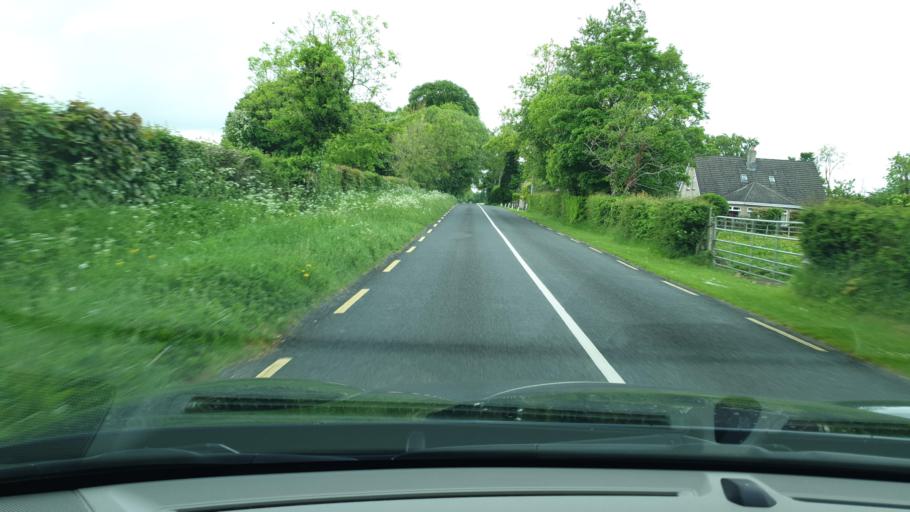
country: IE
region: Leinster
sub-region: An Mhi
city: Ratoath
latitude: 53.5144
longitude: -6.4686
